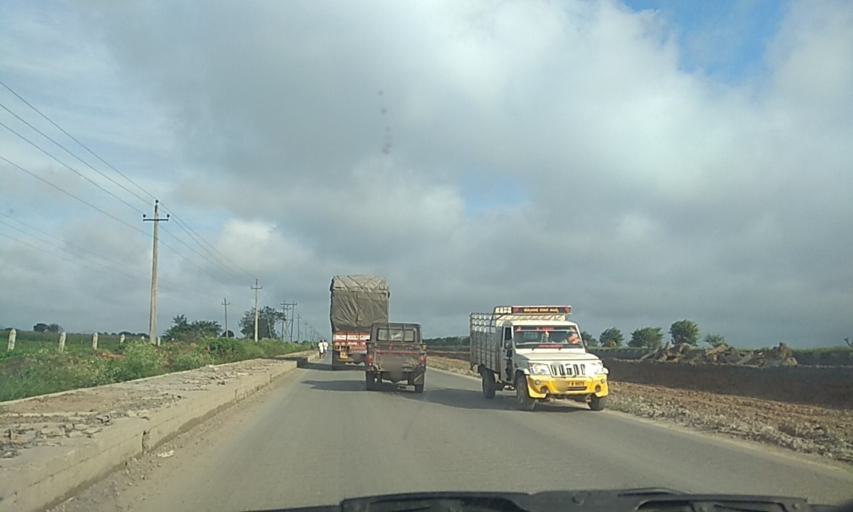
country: IN
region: Karnataka
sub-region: Haveri
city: Savanur
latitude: 14.8844
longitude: 75.3057
